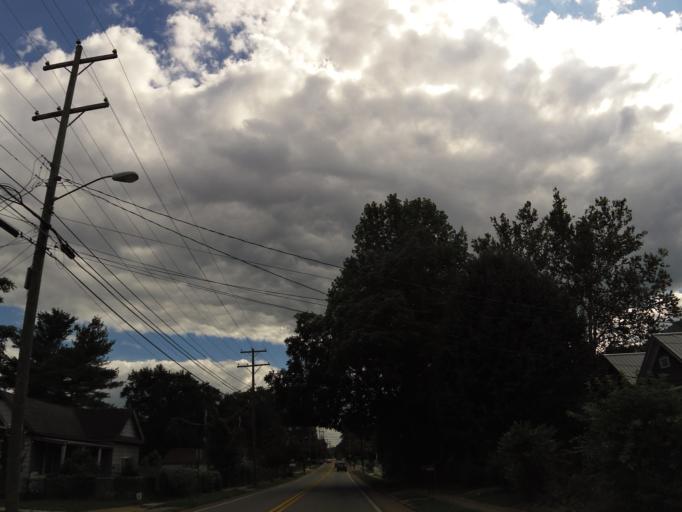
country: US
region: Tennessee
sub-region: Hamilton County
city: Lookout Mountain
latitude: 34.9879
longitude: -85.3315
